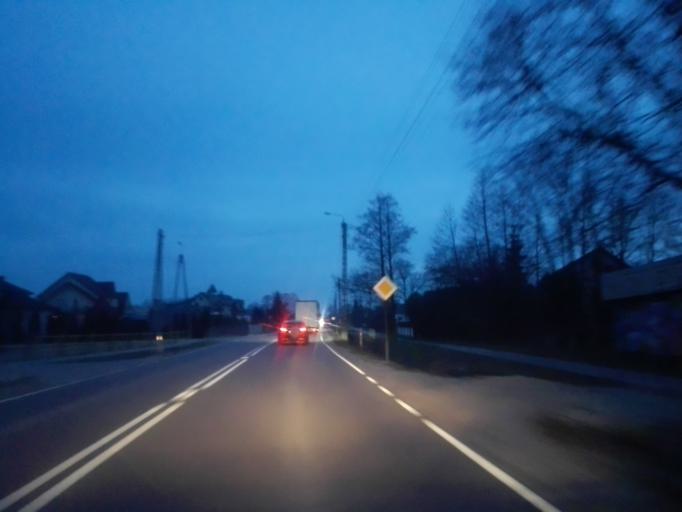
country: PL
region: Podlasie
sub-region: Lomza
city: Lomza
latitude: 53.1377
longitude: 22.0432
